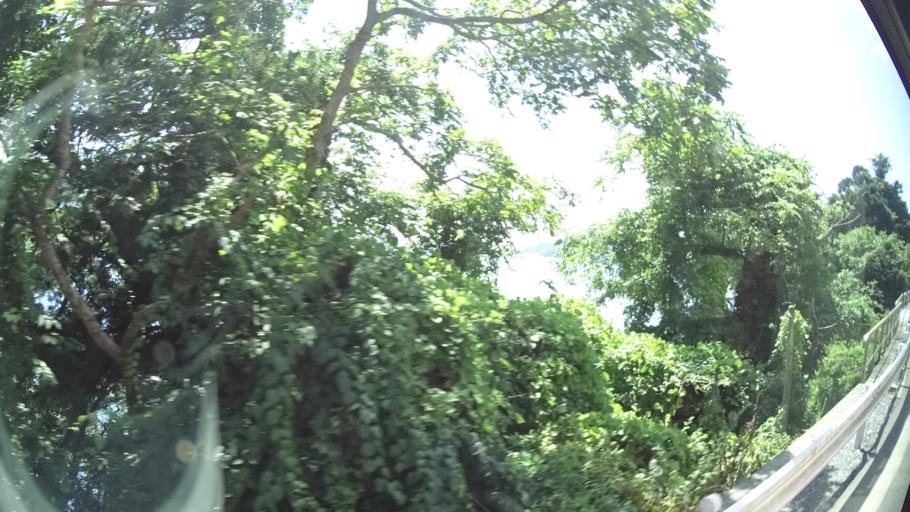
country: JP
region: Iwate
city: Ofunato
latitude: 39.0334
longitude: 141.7166
